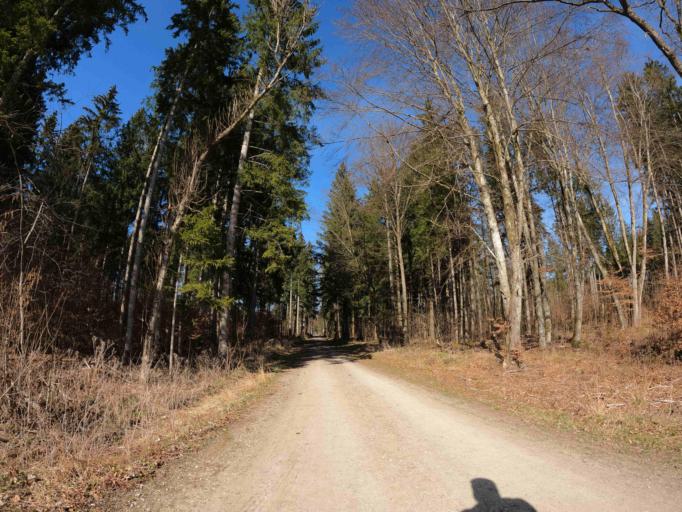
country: DE
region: Bavaria
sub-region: Upper Bavaria
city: Sauerlach
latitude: 48.0020
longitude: 11.6335
